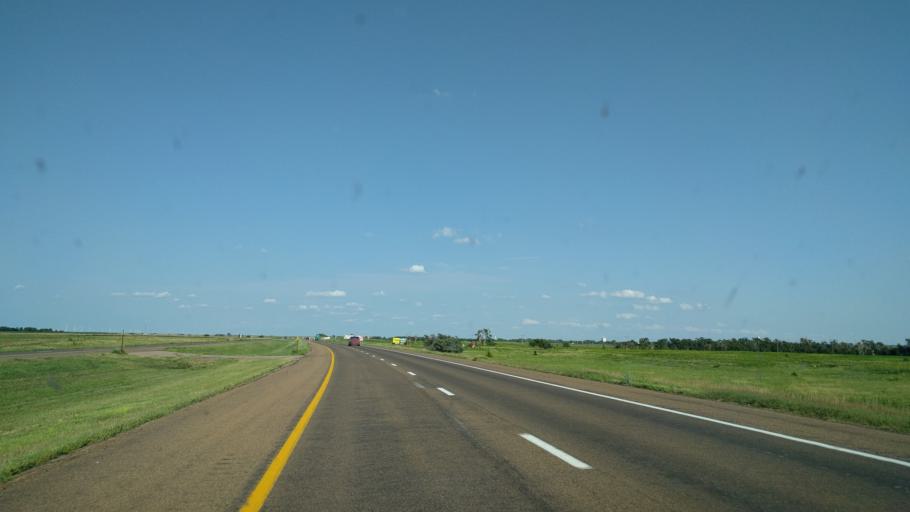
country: US
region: Kansas
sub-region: Ellis County
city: Ellis
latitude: 38.9502
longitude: -99.5937
